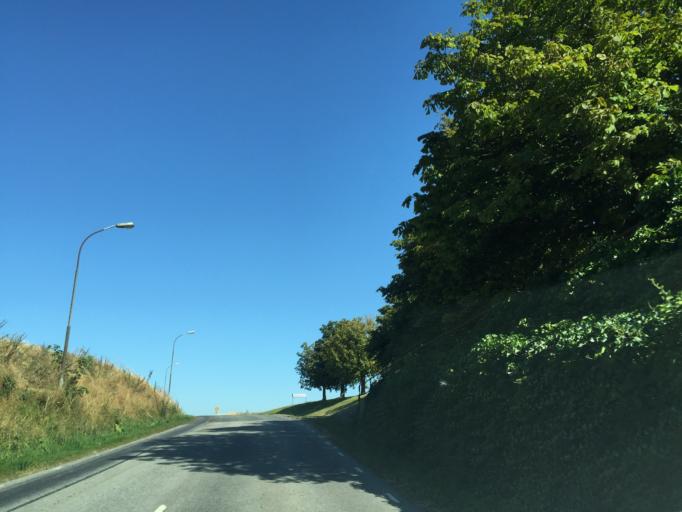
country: SE
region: Skane
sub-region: Ystads Kommun
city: Kopingebro
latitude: 55.4454
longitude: 14.1214
